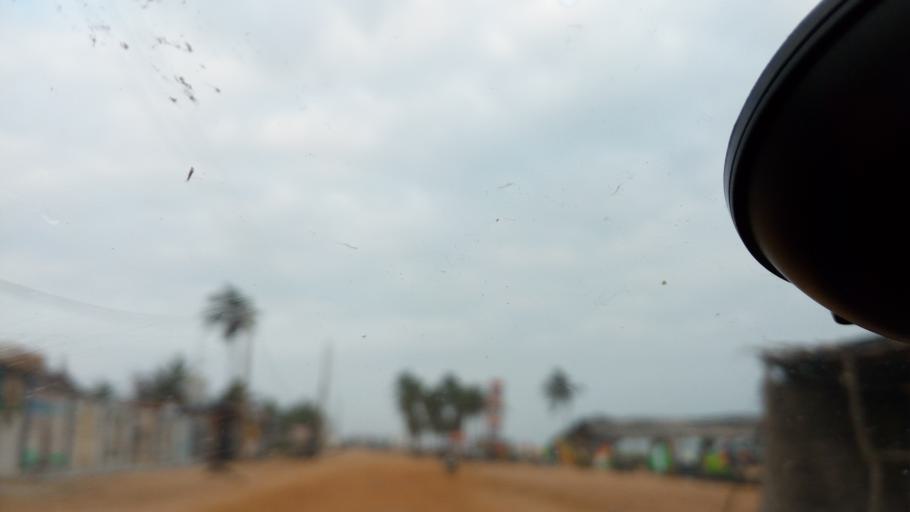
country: BJ
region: Atlantique
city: Ouidah
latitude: 6.3222
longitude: 2.0831
